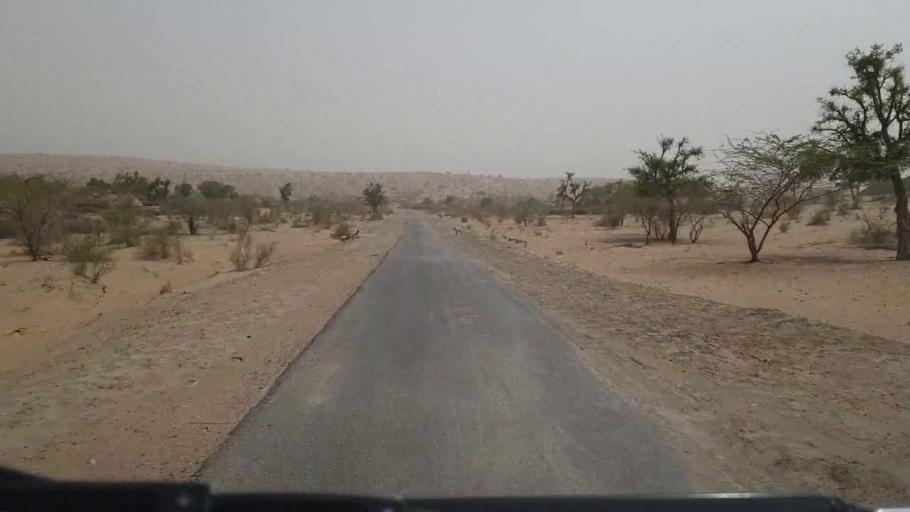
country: PK
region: Sindh
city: Islamkot
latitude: 25.2685
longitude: 70.6507
